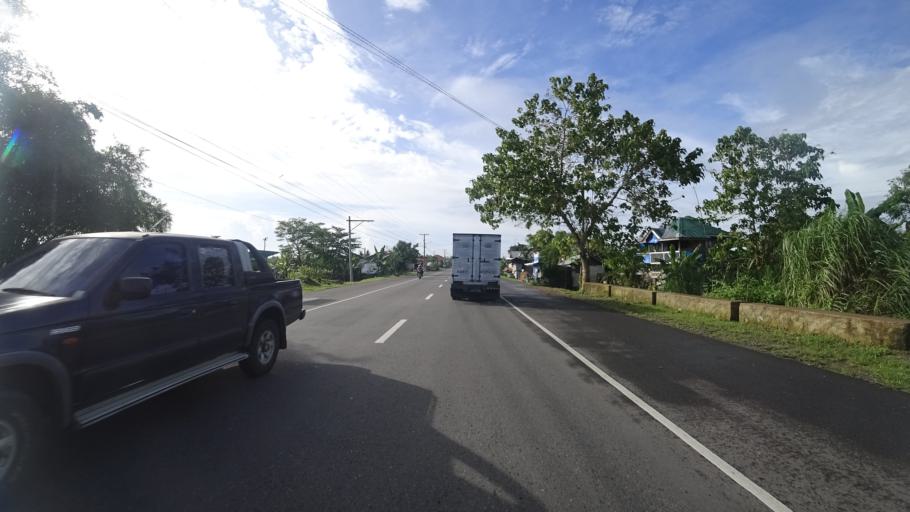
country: PH
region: Eastern Visayas
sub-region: Province of Leyte
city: Tanauan
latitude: 11.1246
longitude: 125.0132
